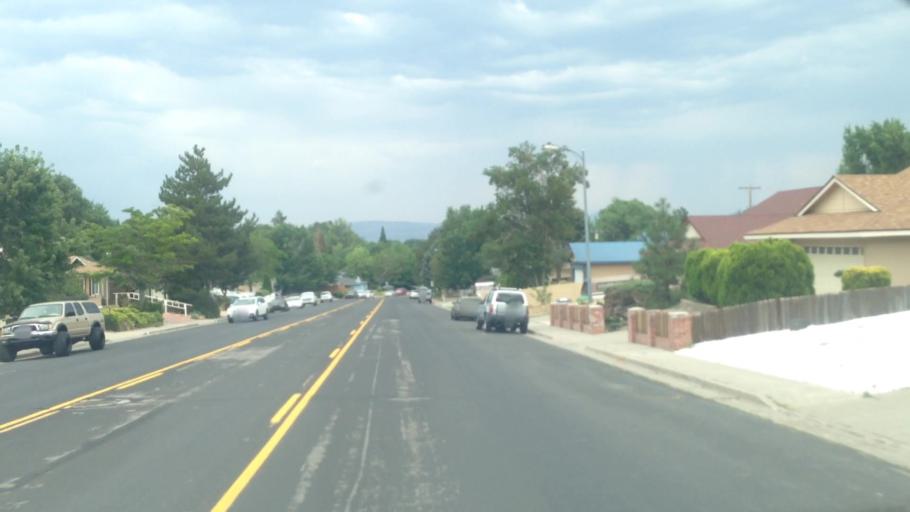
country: US
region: Nevada
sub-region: Washoe County
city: Reno
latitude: 39.5367
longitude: -119.8410
